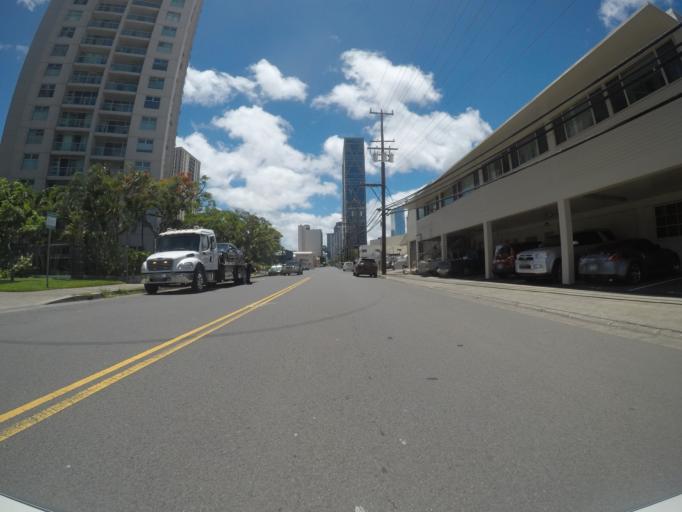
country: US
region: Hawaii
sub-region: Honolulu County
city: Honolulu
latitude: 21.2945
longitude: -157.8498
